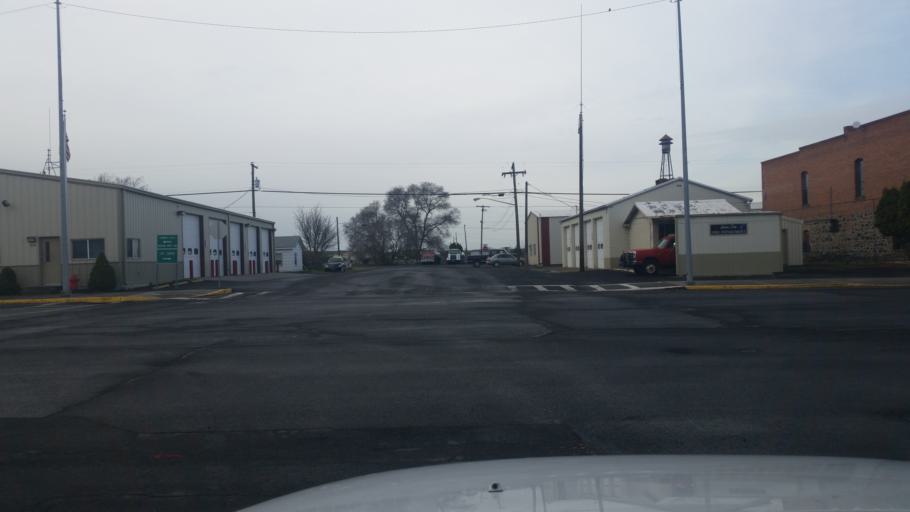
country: US
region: Washington
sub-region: Grant County
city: Soap Lake
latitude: 47.6113
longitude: -119.2930
